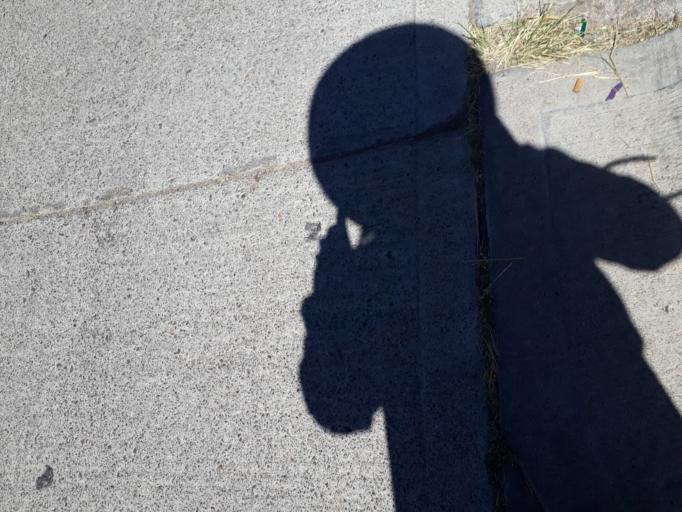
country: MX
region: Aguascalientes
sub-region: Aguascalientes
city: Aguascalientes
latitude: 21.8768
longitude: -102.2417
